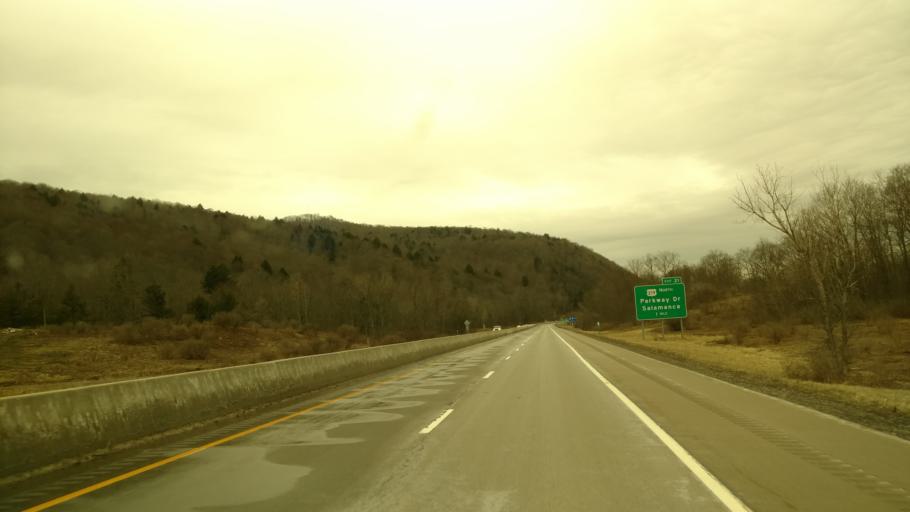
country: US
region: New York
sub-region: Cattaraugus County
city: Salamanca
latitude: 42.1475
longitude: -78.6771
